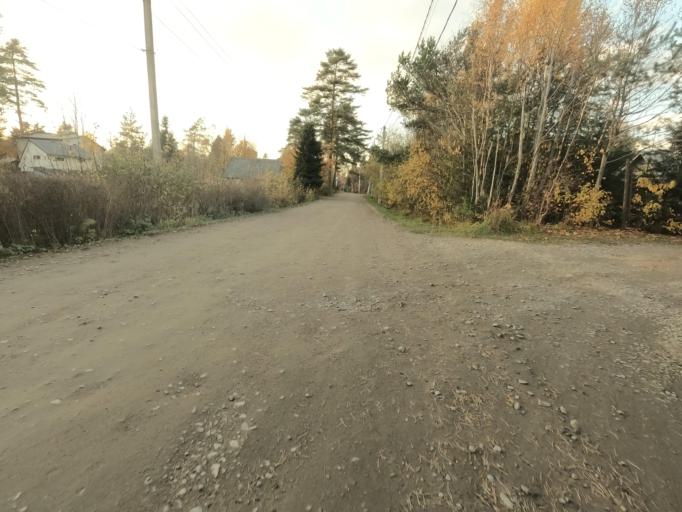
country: RU
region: St.-Petersburg
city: Beloostrov
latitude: 60.1628
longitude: 30.0002
